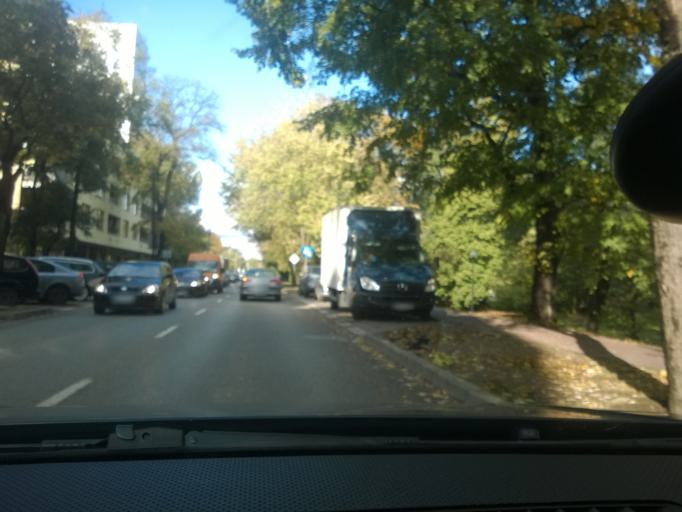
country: PL
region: Masovian Voivodeship
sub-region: Powiat pruszkowski
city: Pruszkow
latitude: 52.1667
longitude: 20.8088
